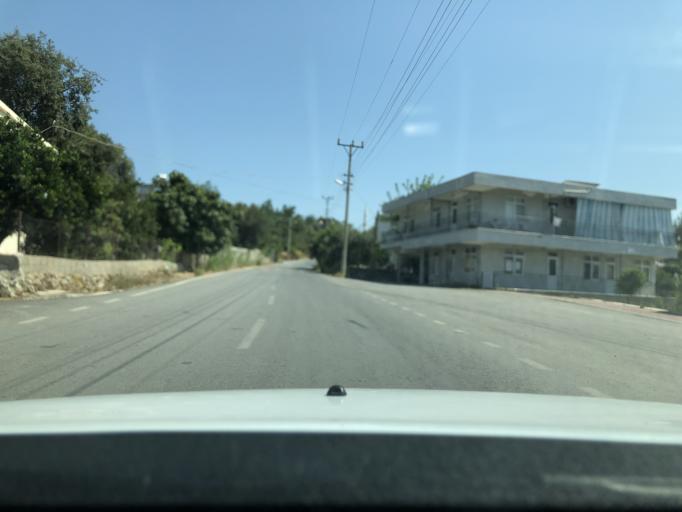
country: TR
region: Antalya
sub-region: Manavgat
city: Manavgat
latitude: 36.8110
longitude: 31.4852
